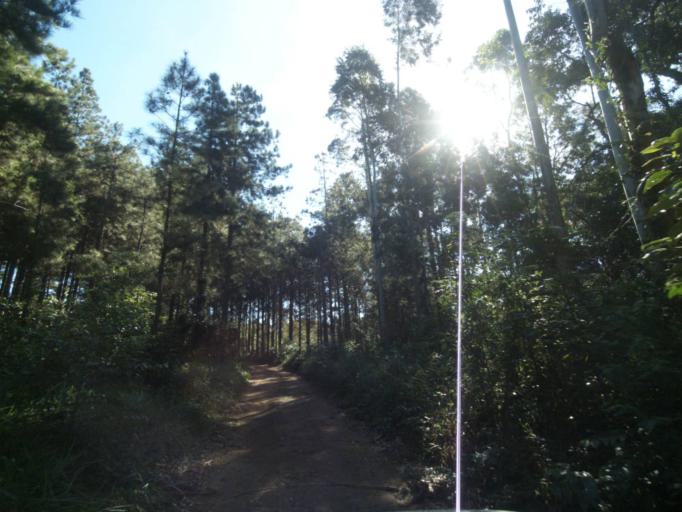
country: BR
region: Parana
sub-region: Tibagi
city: Tibagi
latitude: -24.5523
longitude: -50.4733
